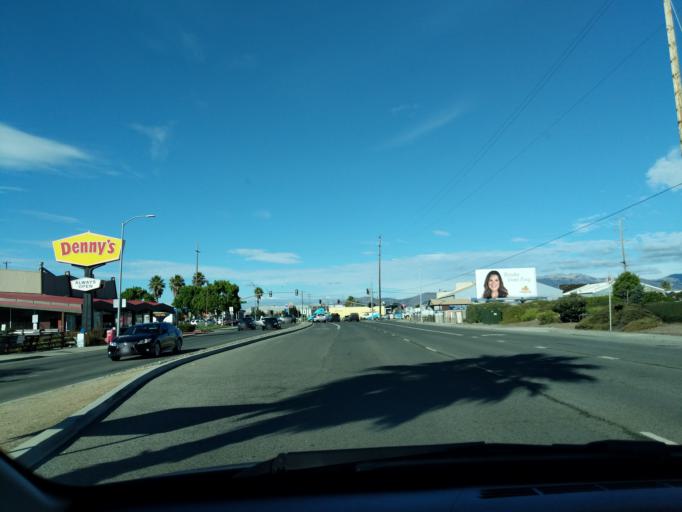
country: US
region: California
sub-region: Monterey County
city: Salinas
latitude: 36.6560
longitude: -121.6364
